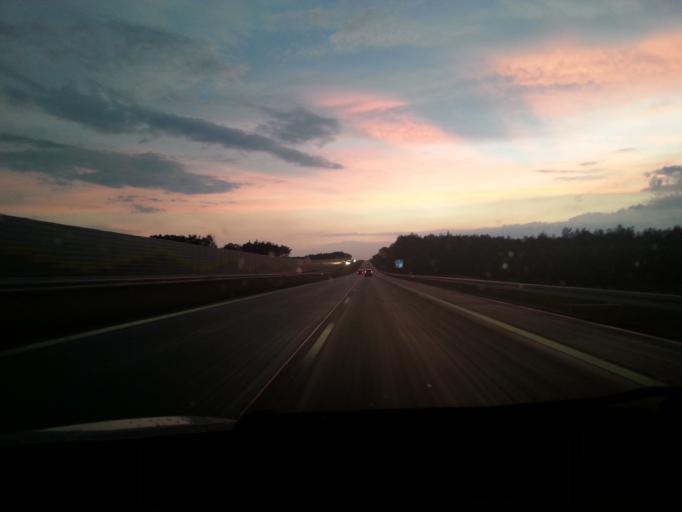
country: PL
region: Lodz Voivodeship
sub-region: Powiat zdunskowolski
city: Zdunska Wola
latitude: 51.5685
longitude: 18.9737
